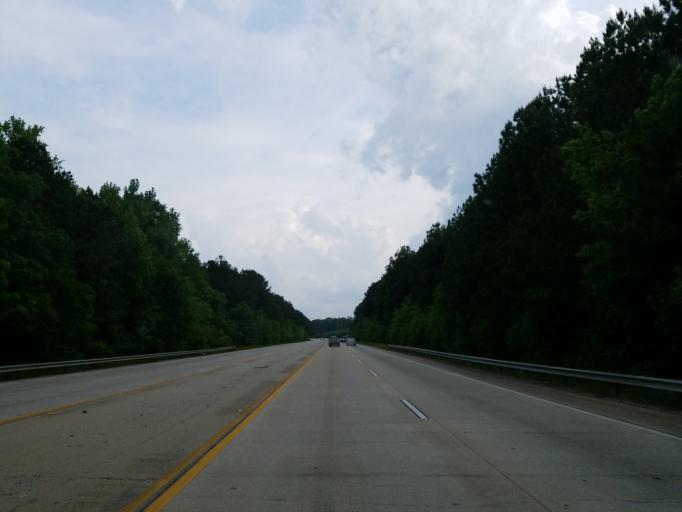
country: US
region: Georgia
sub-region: Cobb County
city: Powder Springs
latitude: 33.8596
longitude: -84.6973
